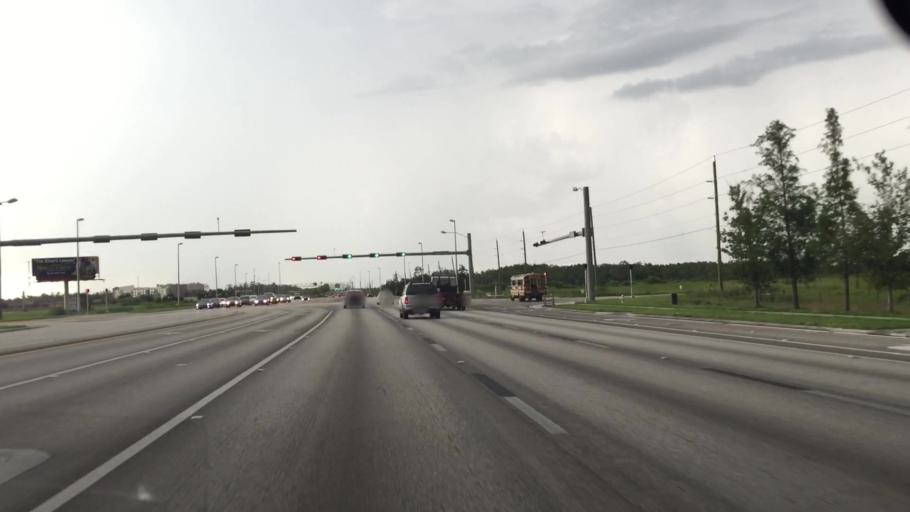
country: US
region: Florida
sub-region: Lee County
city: Tice
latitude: 26.6319
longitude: -81.7914
